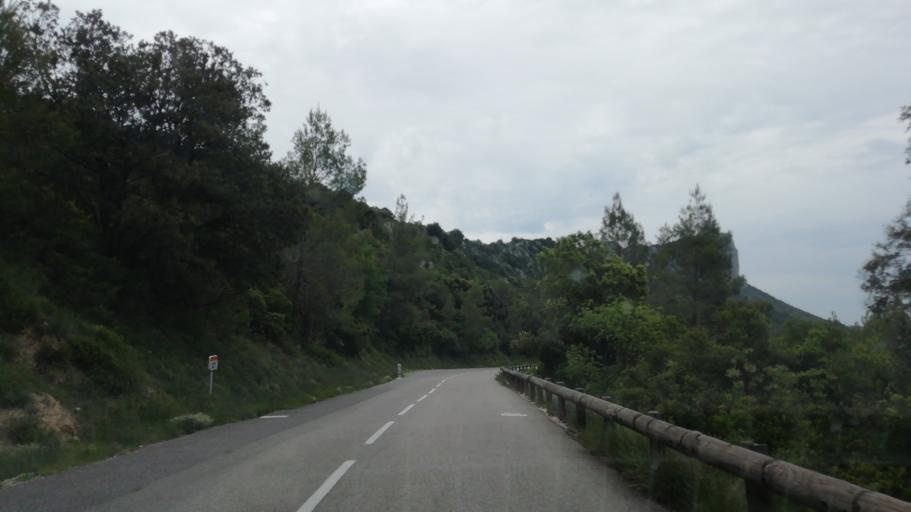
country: FR
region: Languedoc-Roussillon
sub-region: Departement de l'Herault
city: Saint-Mathieu-de-Treviers
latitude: 43.7901
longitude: 3.8087
